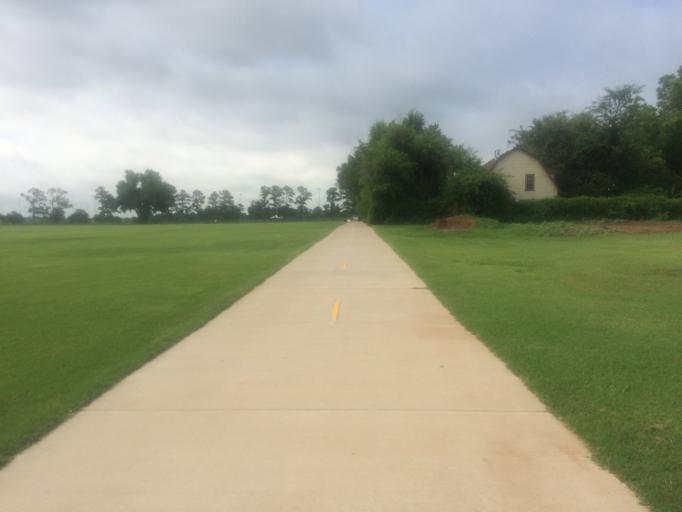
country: US
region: Oklahoma
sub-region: Cleveland County
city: Norman
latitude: 35.1992
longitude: -97.4402
